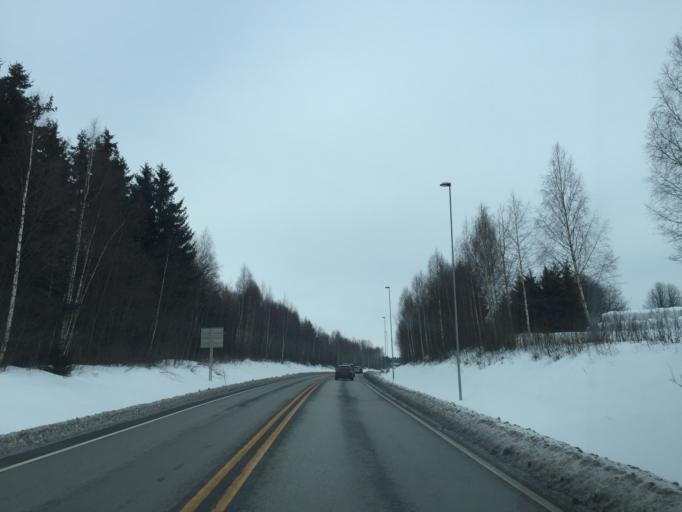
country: NO
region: Hedmark
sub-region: Loten
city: Loten
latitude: 60.7925
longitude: 11.2960
